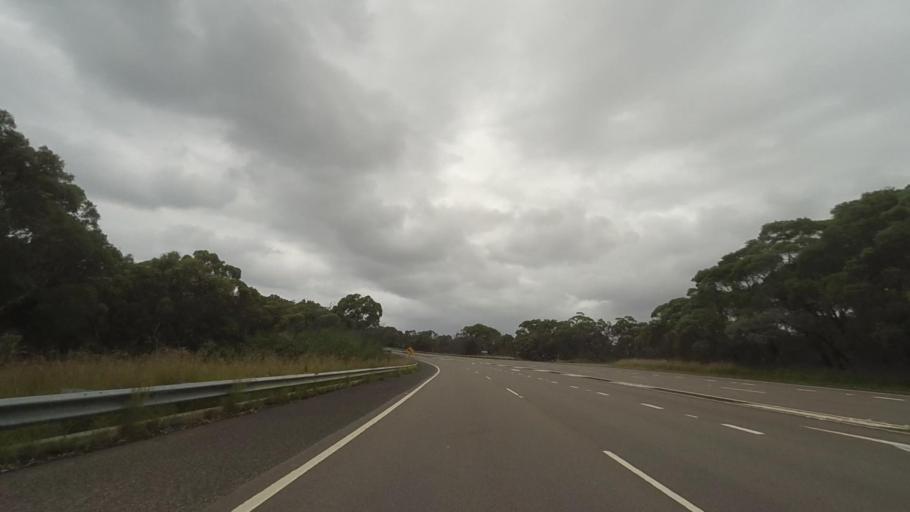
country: AU
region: New South Wales
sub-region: Wyong Shire
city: Kingfisher Shores
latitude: -33.1423
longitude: 151.6102
